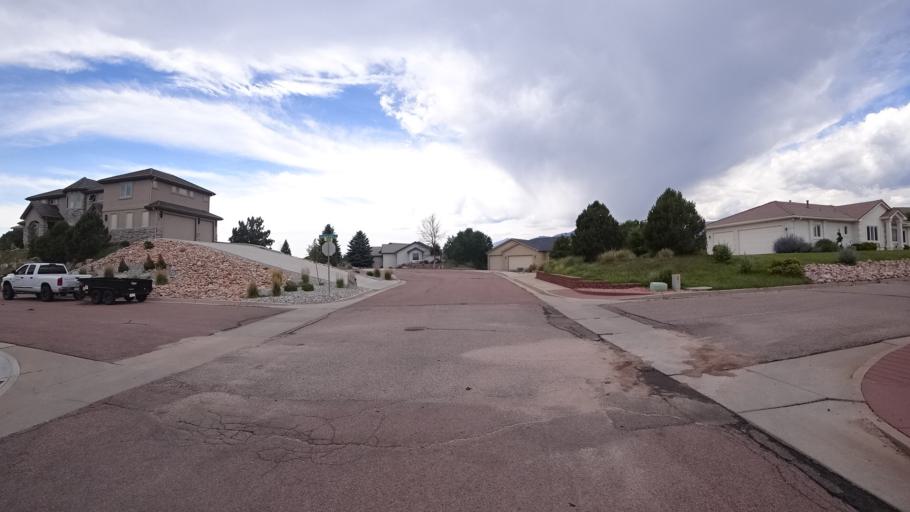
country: US
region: Colorado
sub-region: El Paso County
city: Colorado Springs
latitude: 38.9088
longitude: -104.8331
